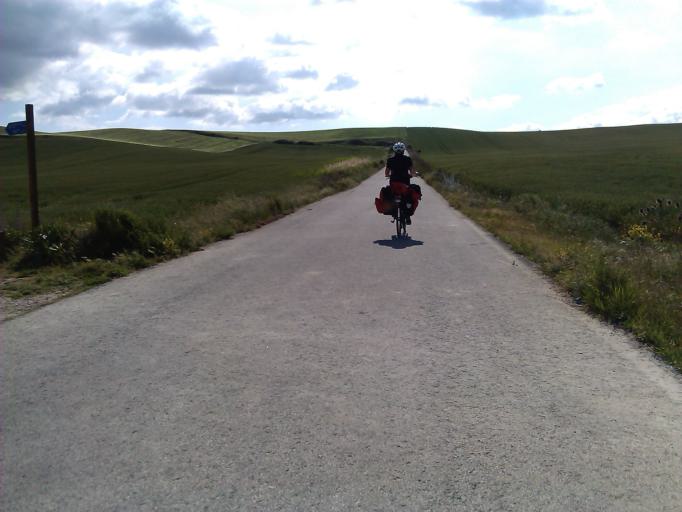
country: ES
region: Navarre
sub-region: Provincia de Navarra
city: Cizur Mayor
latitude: 42.7782
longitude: -1.6897
